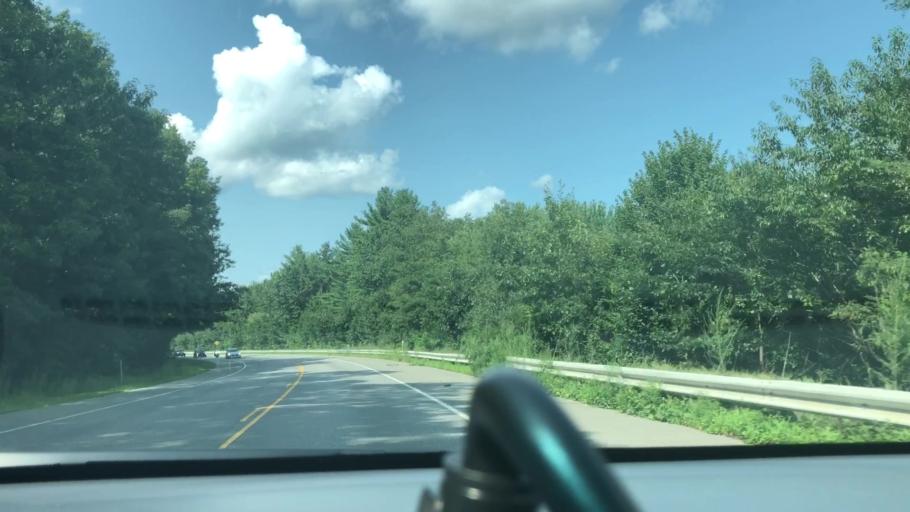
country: US
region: New Hampshire
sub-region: Hillsborough County
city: Pinardville
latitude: 42.9997
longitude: -71.5245
